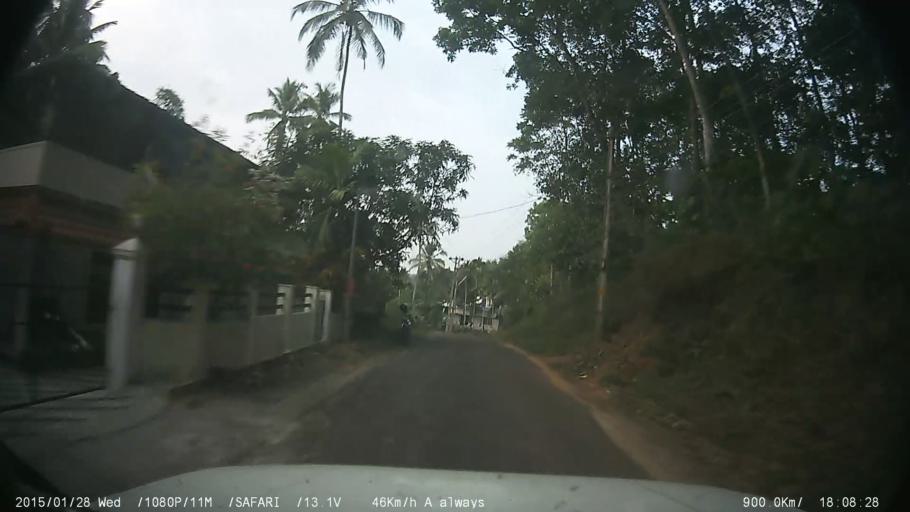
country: IN
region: Kerala
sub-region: Kottayam
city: Palackattumala
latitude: 9.7408
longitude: 76.5752
